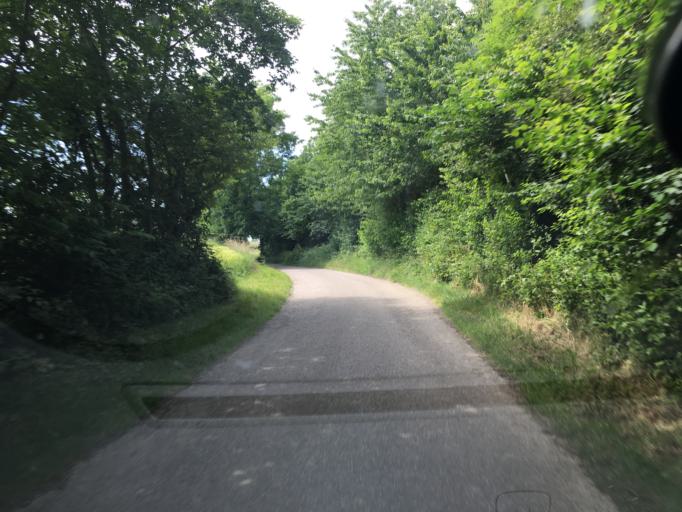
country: DK
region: South Denmark
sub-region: Sonderborg Kommune
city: Dybbol
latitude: 54.9456
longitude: 9.7476
